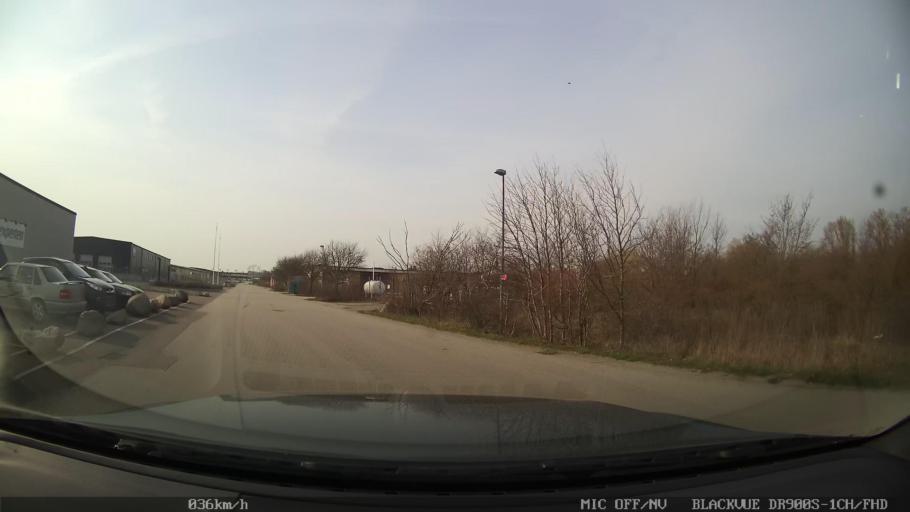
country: SE
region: Skane
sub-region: Ystads Kommun
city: Ystad
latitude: 55.4477
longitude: 13.8498
